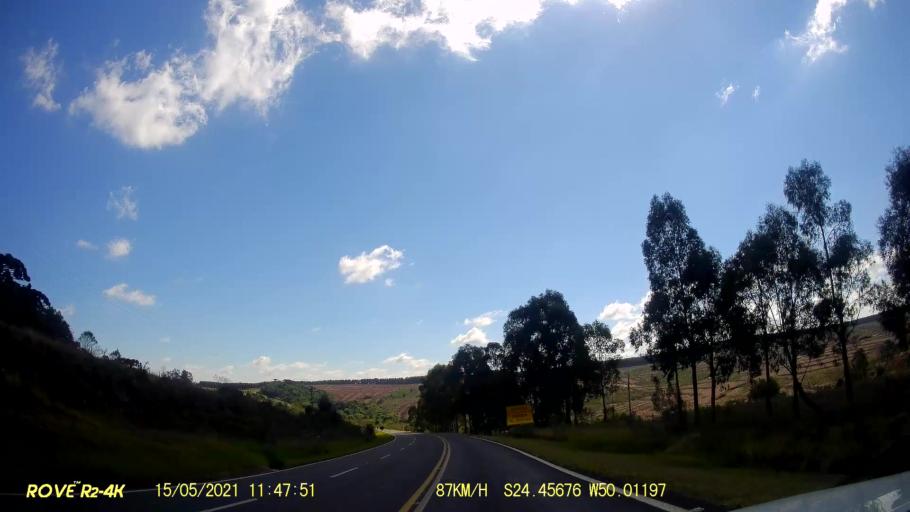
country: BR
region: Parana
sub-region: Pirai Do Sul
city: Pirai do Sul
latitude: -24.4569
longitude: -50.0118
